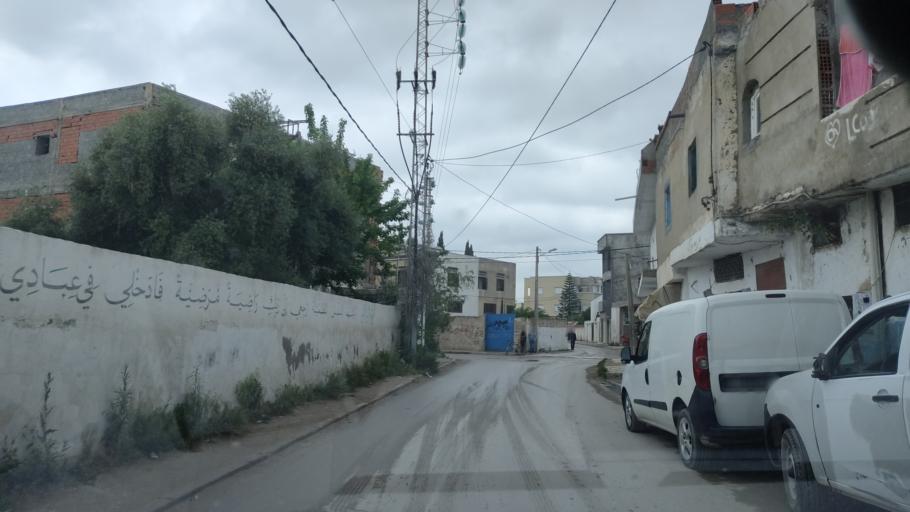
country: TN
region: Ariana
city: Ariana
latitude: 36.8775
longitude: 10.2173
